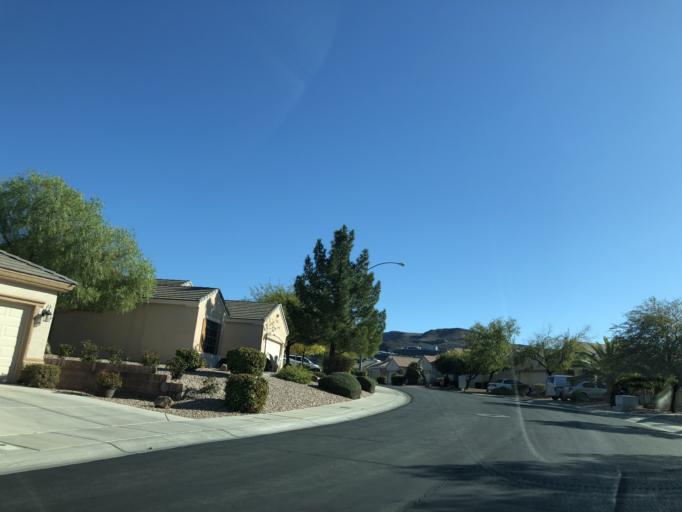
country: US
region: Nevada
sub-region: Clark County
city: Whitney
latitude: 36.0054
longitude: -115.0703
